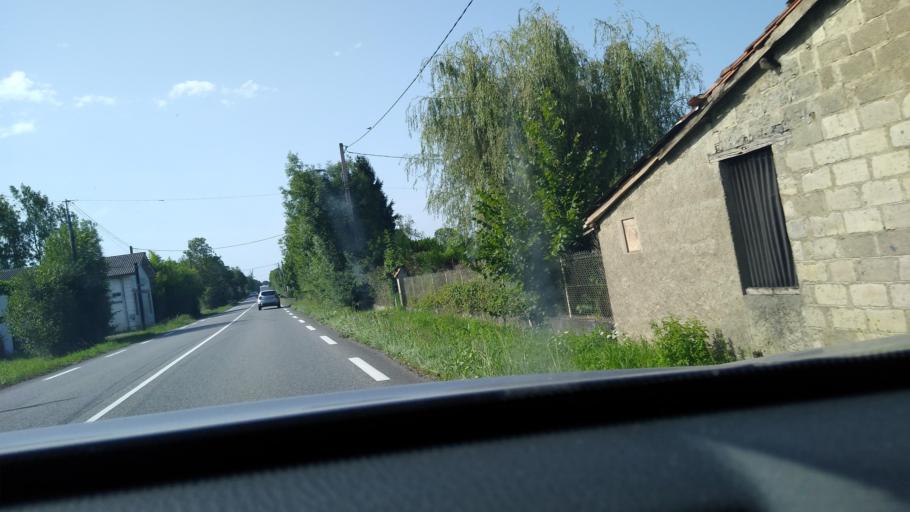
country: FR
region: Midi-Pyrenees
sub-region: Departement de la Haute-Garonne
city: Salies-du-Salat
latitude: 43.0565
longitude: 0.9780
